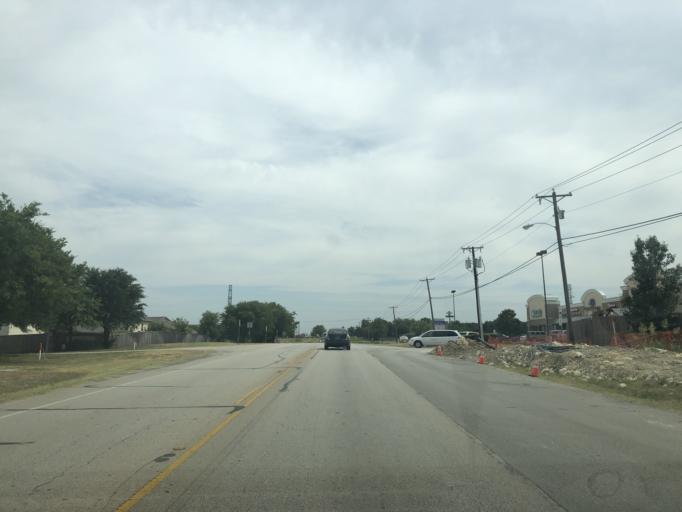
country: US
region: Texas
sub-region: Tarrant County
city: Blue Mound
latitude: 32.8780
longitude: -97.3425
